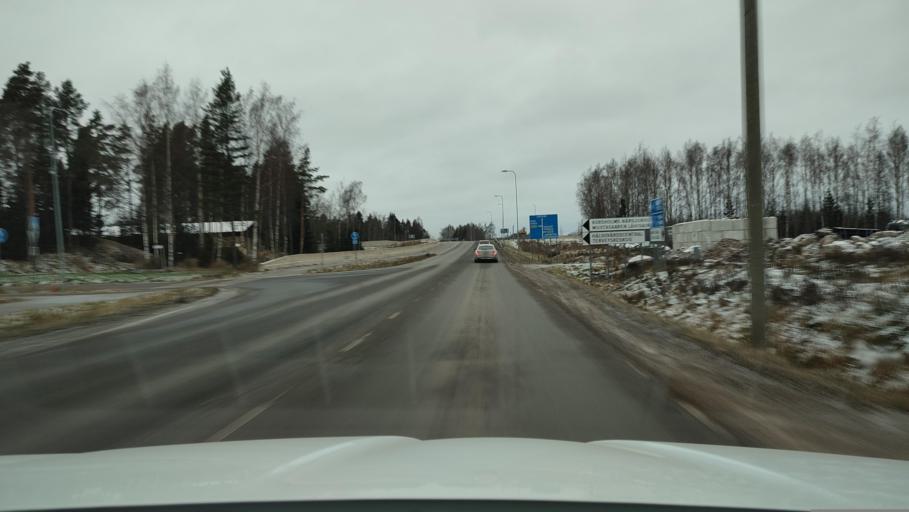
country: FI
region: Ostrobothnia
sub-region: Vaasa
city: Smedsby
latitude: 63.1240
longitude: 21.7050
